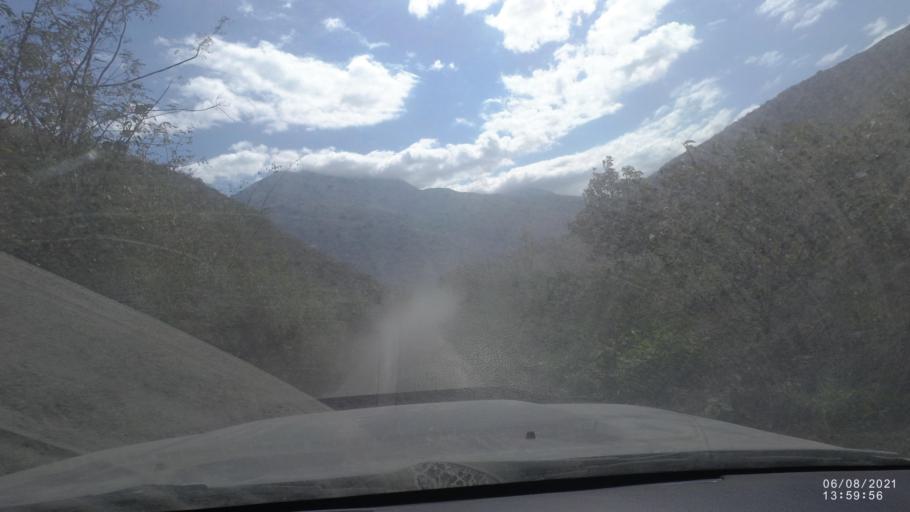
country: BO
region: La Paz
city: Quime
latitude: -16.6444
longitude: -66.7243
